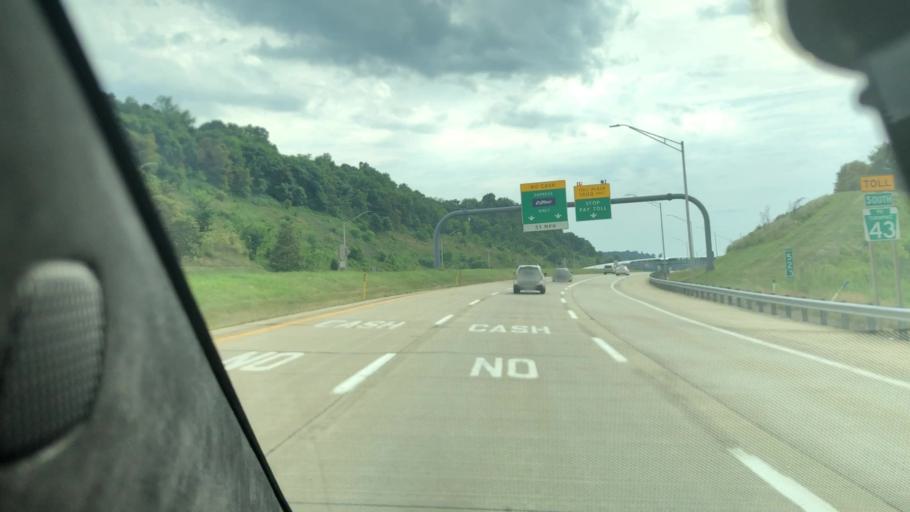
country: US
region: Pennsylvania
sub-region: Allegheny County
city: Jefferson Hills
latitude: 40.2838
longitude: -79.9206
